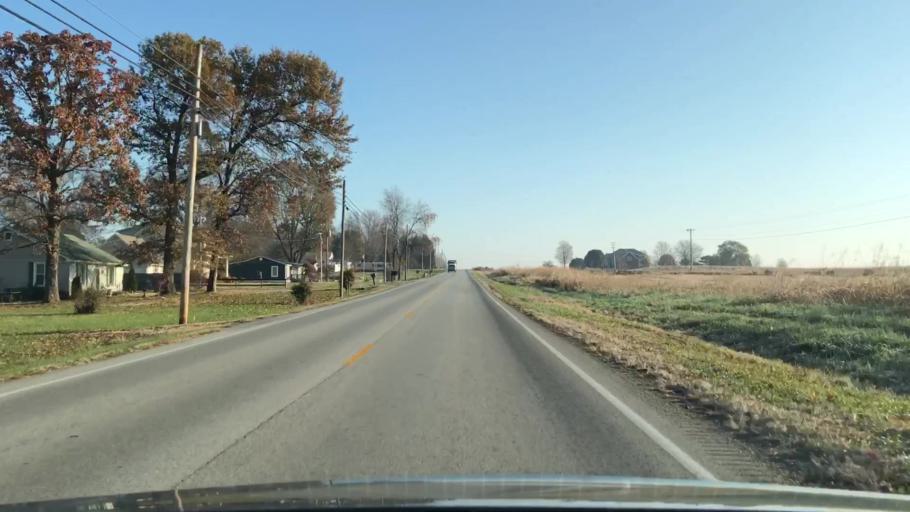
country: US
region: Kentucky
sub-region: Warren County
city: Bowling Green
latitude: 37.0450
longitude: -86.3220
